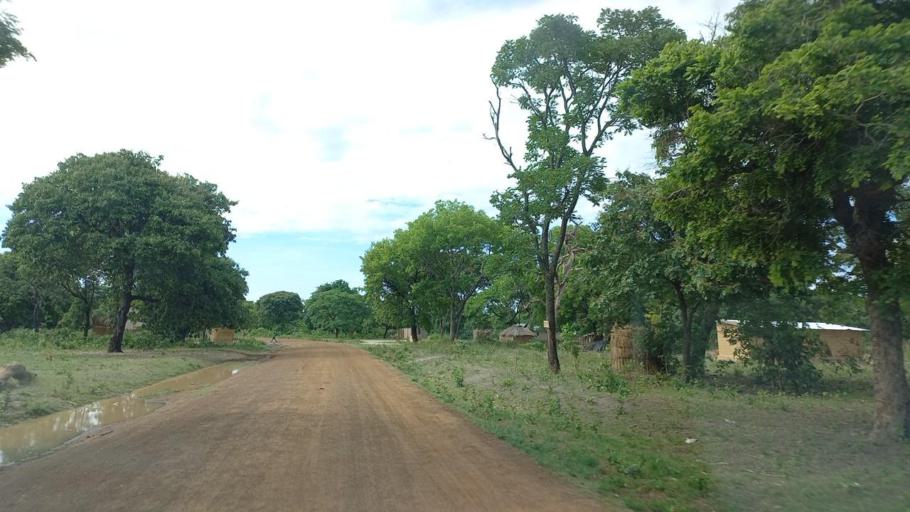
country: ZM
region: North-Western
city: Kabompo
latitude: -13.4599
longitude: 24.4270
